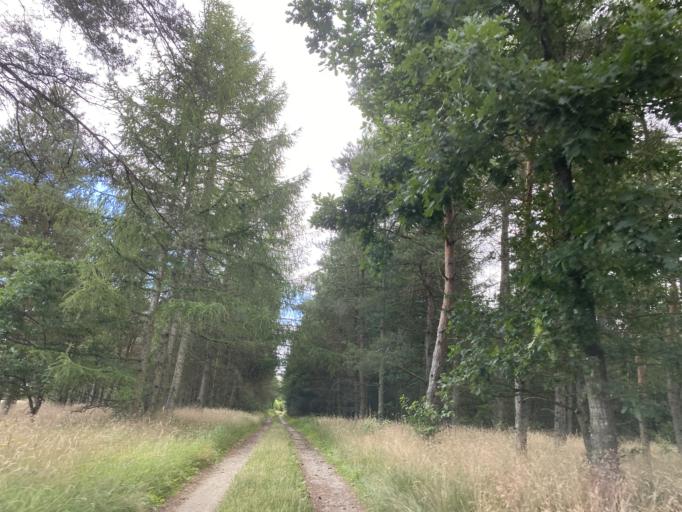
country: DK
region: Central Jutland
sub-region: Viborg Kommune
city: Bjerringbro
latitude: 56.2730
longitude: 9.6551
